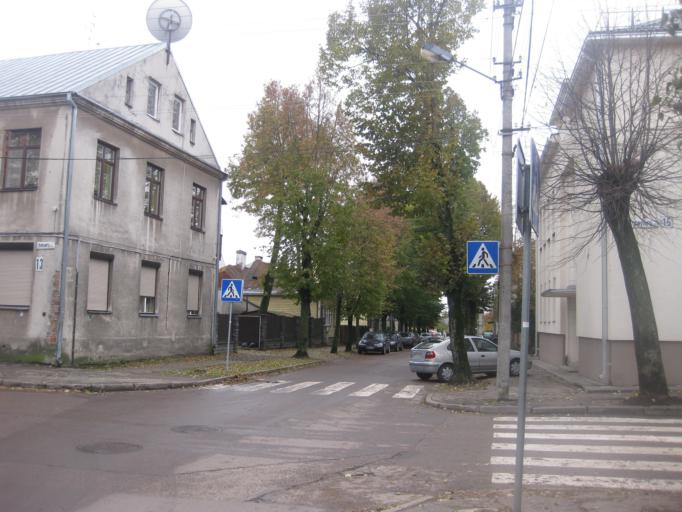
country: LT
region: Kauno apskritis
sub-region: Kaunas
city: Kaunas
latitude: 54.9076
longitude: 23.9212
